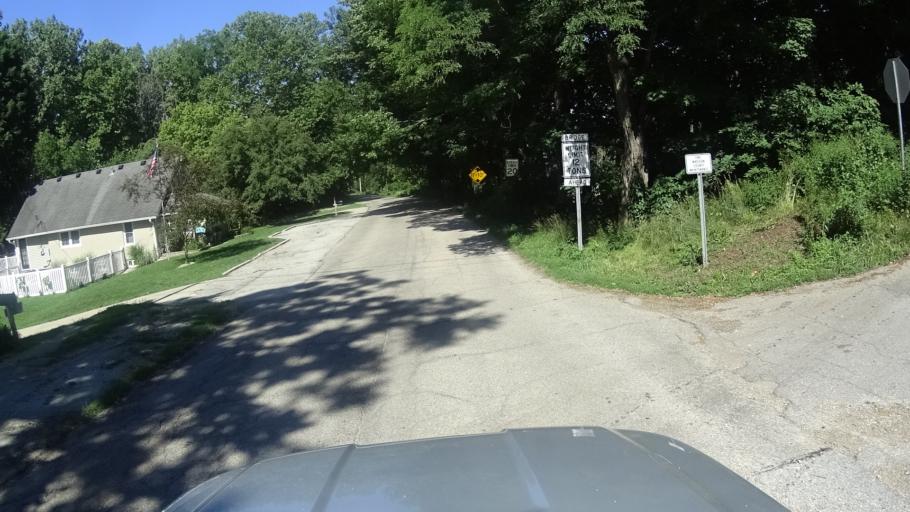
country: US
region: Indiana
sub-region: Madison County
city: Pendleton
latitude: 40.0086
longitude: -85.7322
